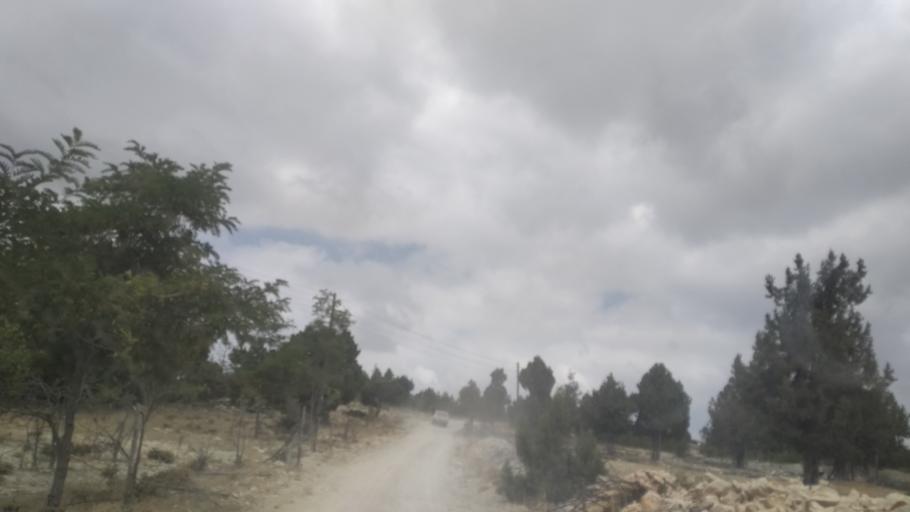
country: TR
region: Mersin
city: Sarikavak
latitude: 36.5688
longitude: 33.7650
